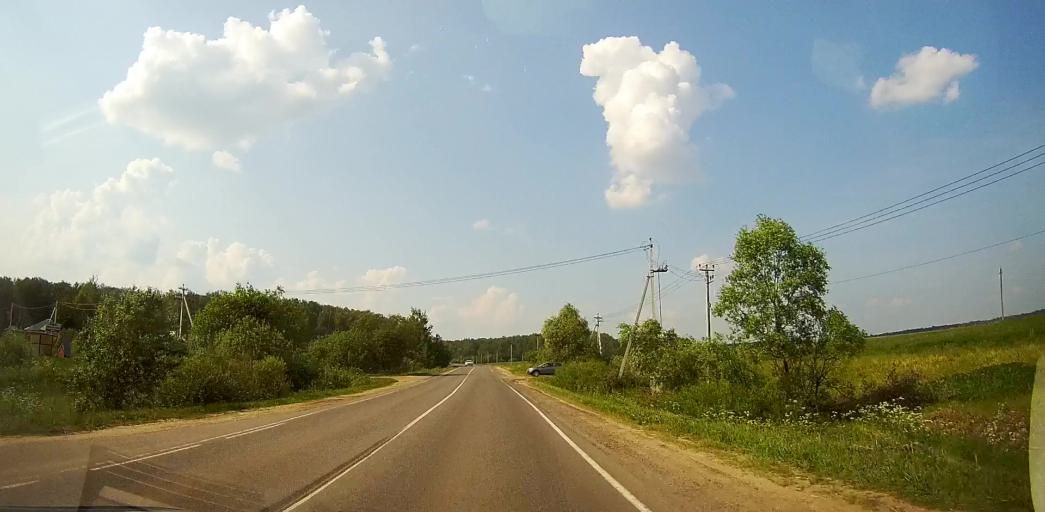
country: RU
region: Moskovskaya
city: Il'inskoye
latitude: 55.2061
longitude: 37.9615
